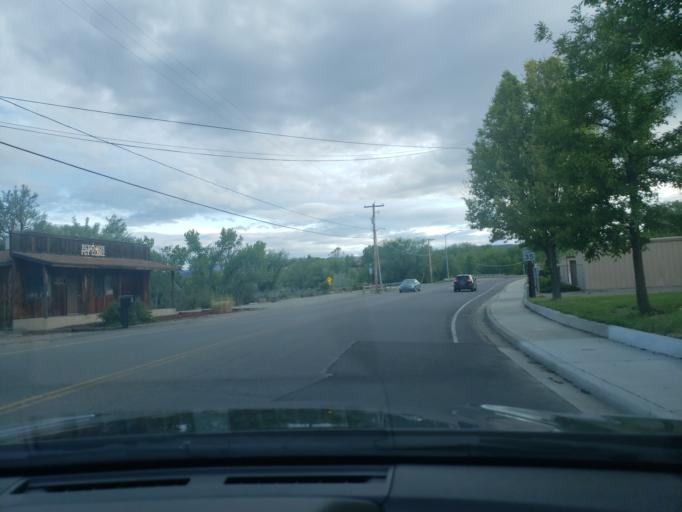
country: US
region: Colorado
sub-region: Mesa County
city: Grand Junction
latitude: 39.0644
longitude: -108.5856
